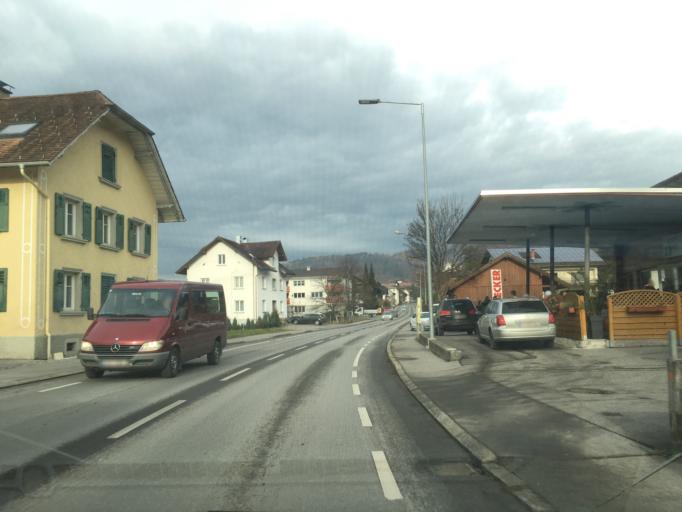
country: AT
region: Vorarlberg
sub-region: Politischer Bezirk Feldkirch
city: Weiler
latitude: 47.2982
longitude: 9.6511
